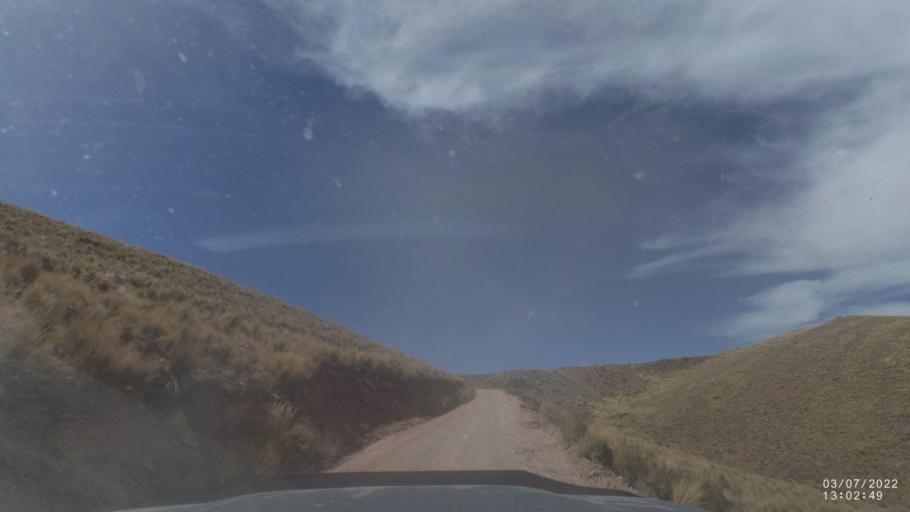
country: BO
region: Cochabamba
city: Colchani
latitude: -17.7066
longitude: -66.6903
